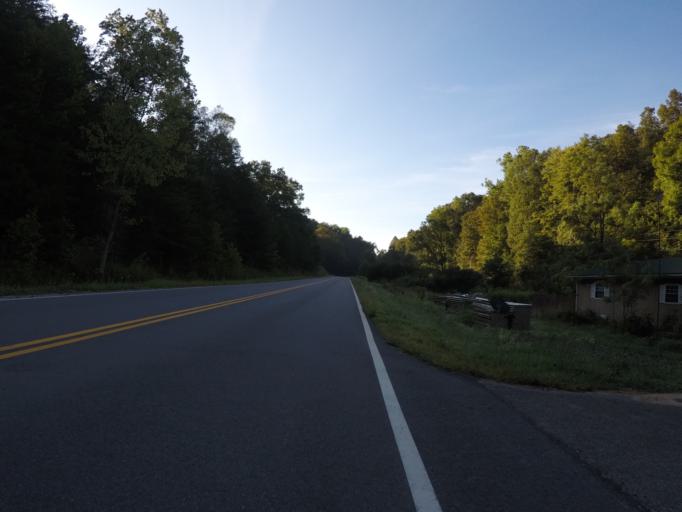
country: US
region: Ohio
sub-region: Lawrence County
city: Coal Grove
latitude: 38.6053
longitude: -82.5711
